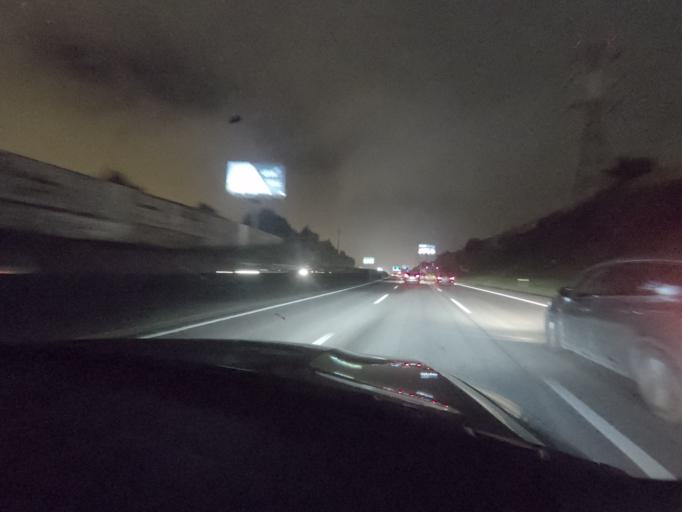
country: PT
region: Lisbon
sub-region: Vila Franca de Xira
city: Vialonga
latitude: 38.8621
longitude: -9.0814
